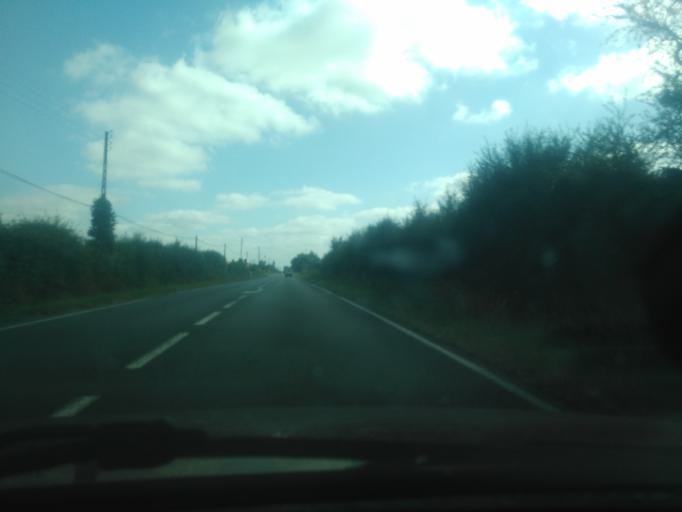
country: FR
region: Pays de la Loire
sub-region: Departement de la Vendee
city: La Ferriere
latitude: 46.7368
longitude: -1.2793
